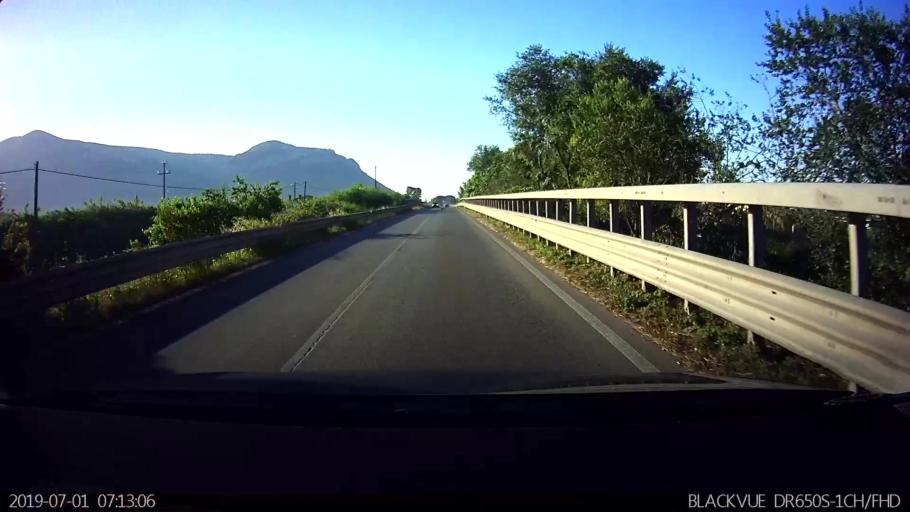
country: IT
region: Latium
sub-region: Provincia di Latina
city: Borgo Hermada
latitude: 41.3299
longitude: 13.1733
